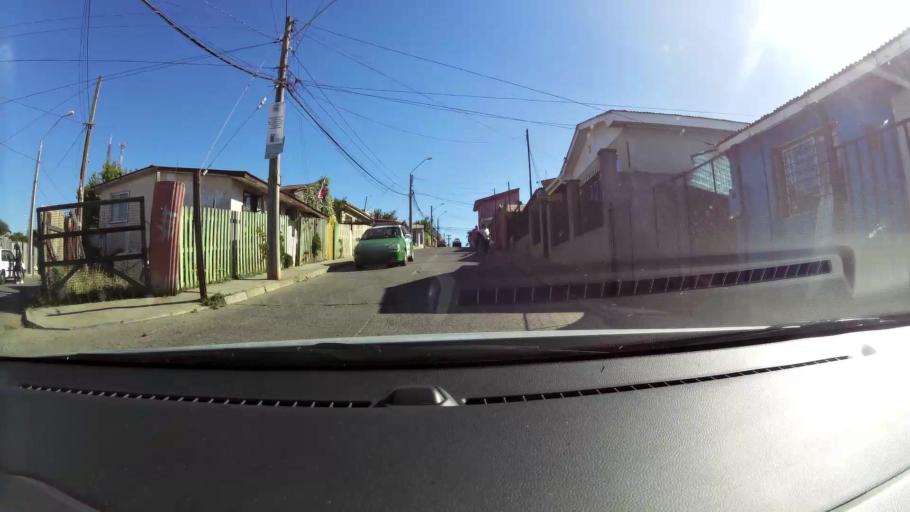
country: CL
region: Valparaiso
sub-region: Provincia de Valparaiso
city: Vina del Mar
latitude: -33.0462
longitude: -71.5627
